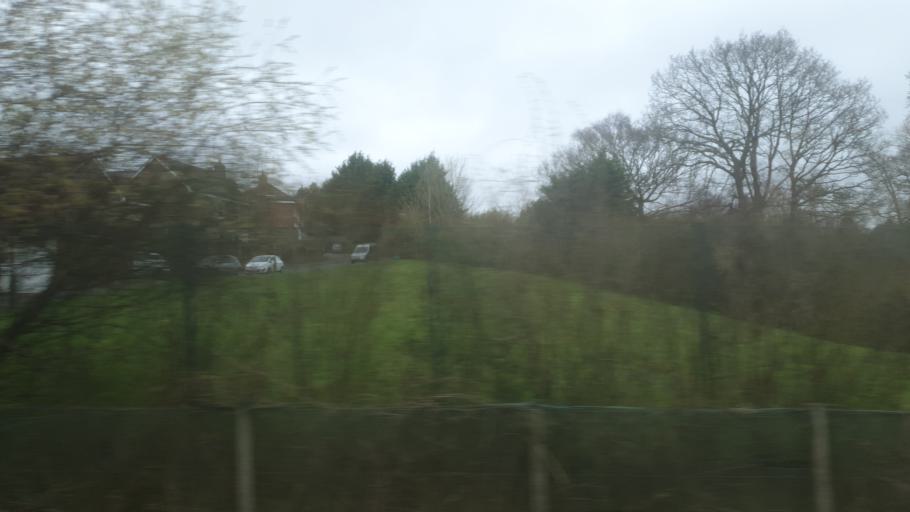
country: GB
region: England
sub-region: West Sussex
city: Pulborough
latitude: 50.9652
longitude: -0.4988
